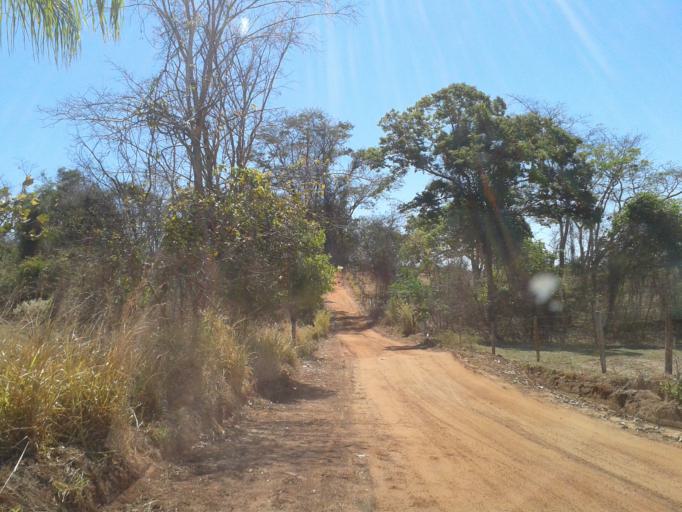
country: BR
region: Minas Gerais
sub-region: Ituiutaba
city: Ituiutaba
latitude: -19.0856
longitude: -49.3015
